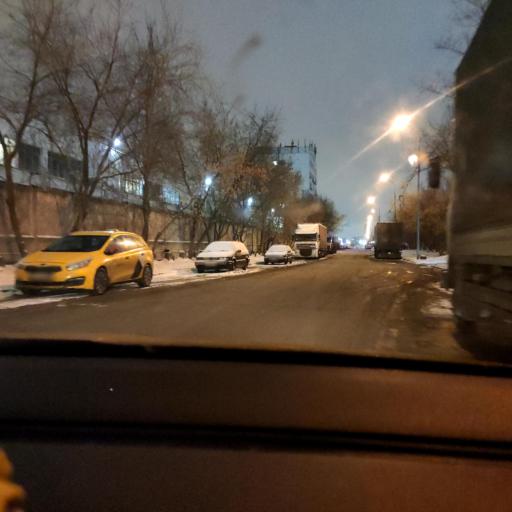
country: RU
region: Moscow
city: Tekstil'shchiki
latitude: 55.7025
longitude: 37.7174
